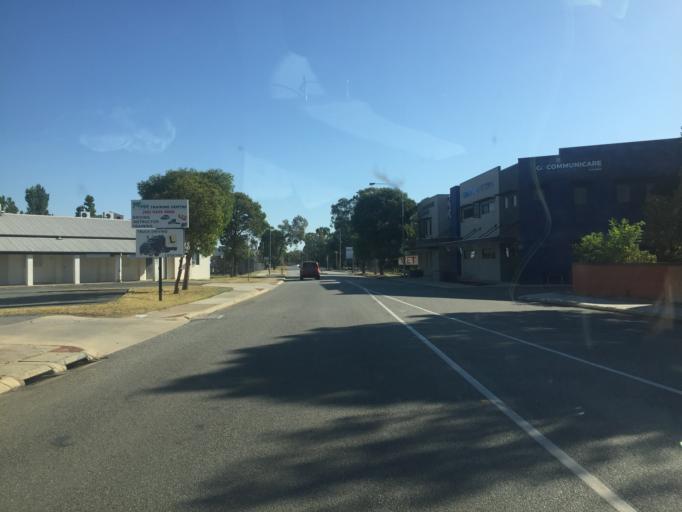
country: AU
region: Western Australia
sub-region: Gosnells
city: Kenwick
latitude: -32.0373
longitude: 115.9683
